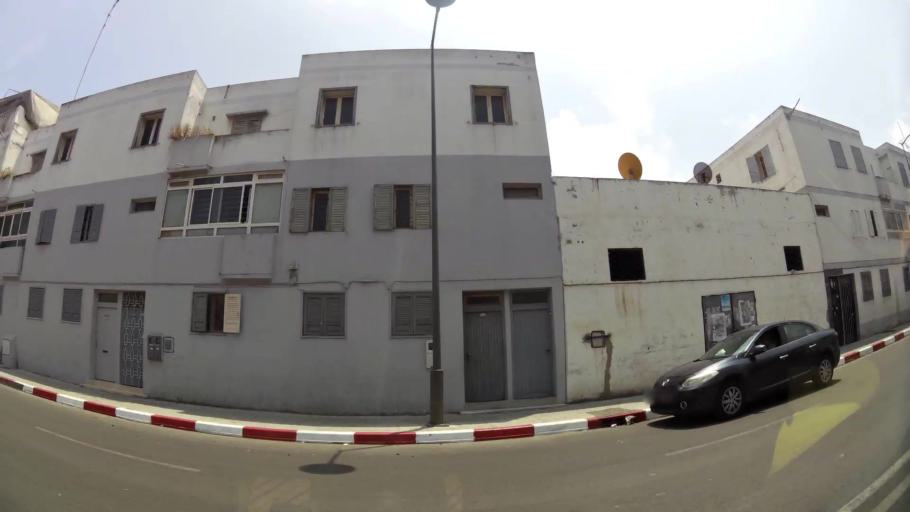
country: MA
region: Rabat-Sale-Zemmour-Zaer
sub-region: Rabat
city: Rabat
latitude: 33.9831
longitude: -6.8801
